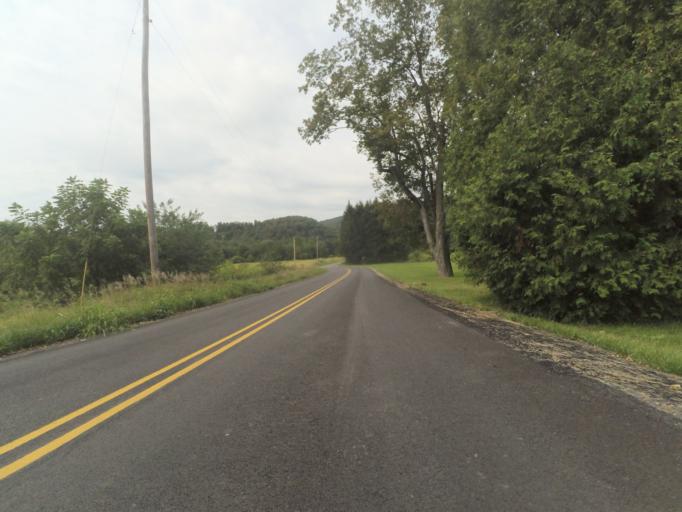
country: US
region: Pennsylvania
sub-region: Huntingdon County
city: McConnellstown
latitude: 40.5890
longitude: -78.1008
